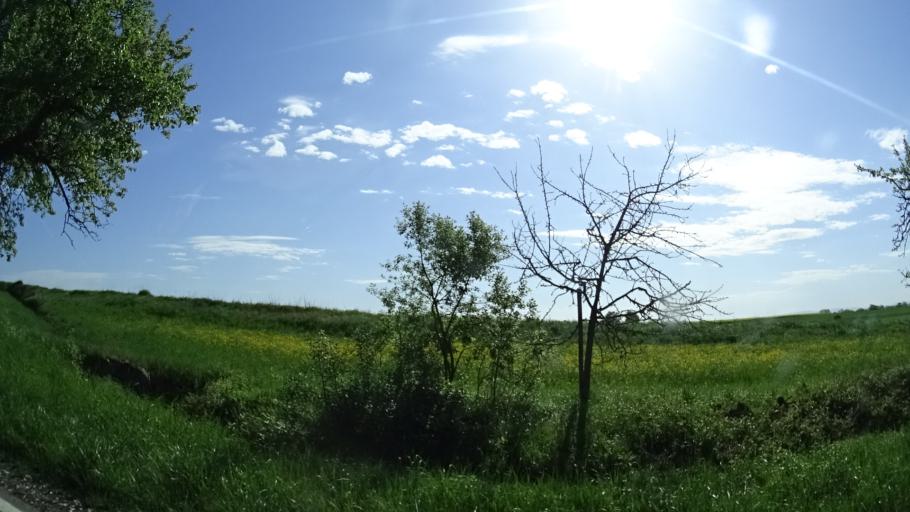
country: DE
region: Baden-Wuerttemberg
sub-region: Regierungsbezirk Stuttgart
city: Motzingen
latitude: 48.5003
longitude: 8.7740
